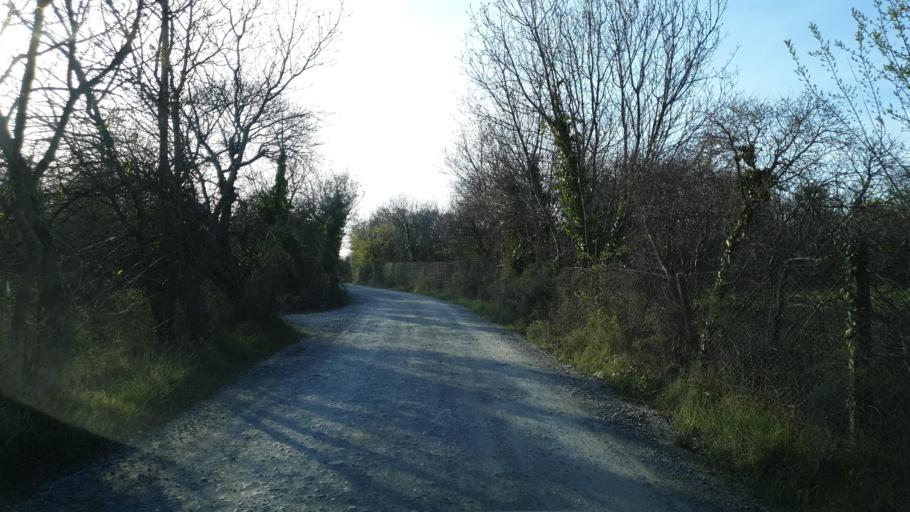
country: IT
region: Friuli Venezia Giulia
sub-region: Provincia di Trieste
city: Prosecco-Contovello
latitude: 45.7161
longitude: 13.7459
